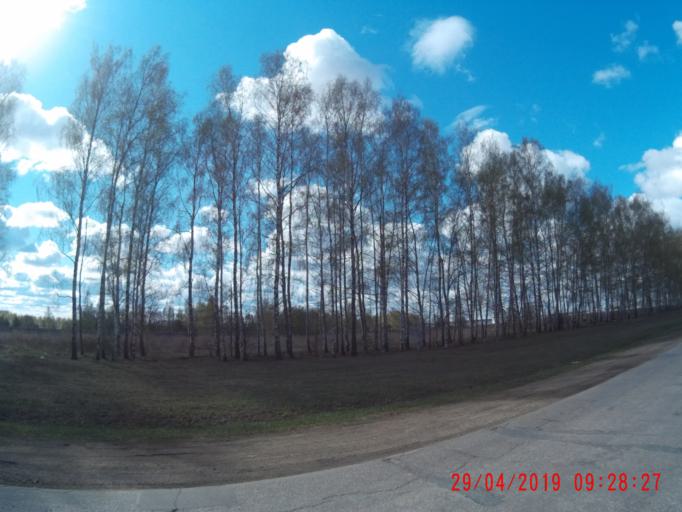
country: RU
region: Nizjnij Novgorod
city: Diveyevo
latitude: 55.0474
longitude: 43.2741
